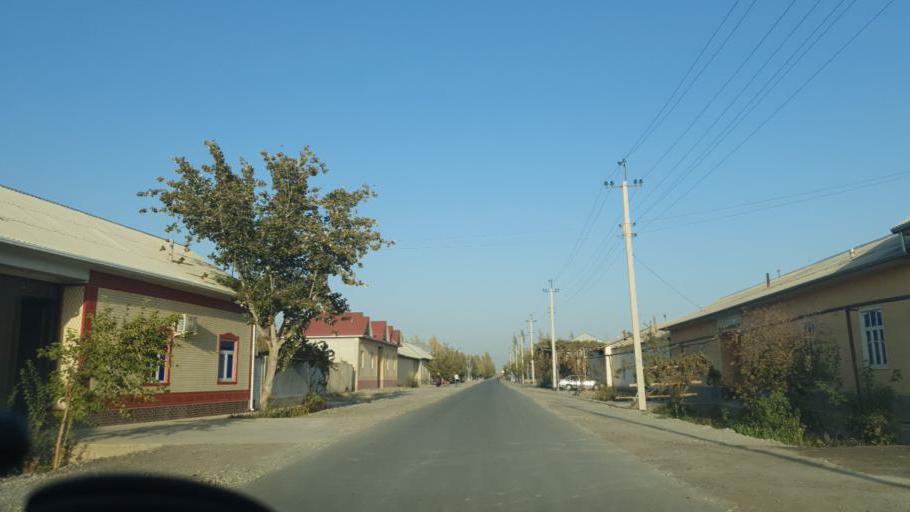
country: UZ
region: Fergana
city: Beshariq
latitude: 40.4625
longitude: 70.5455
